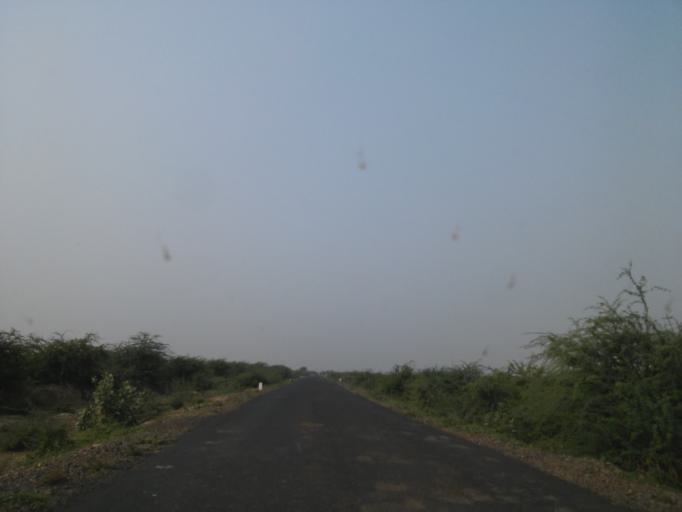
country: IN
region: Gujarat
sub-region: Kachchh
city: Bhuj
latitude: 23.6674
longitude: 69.6974
